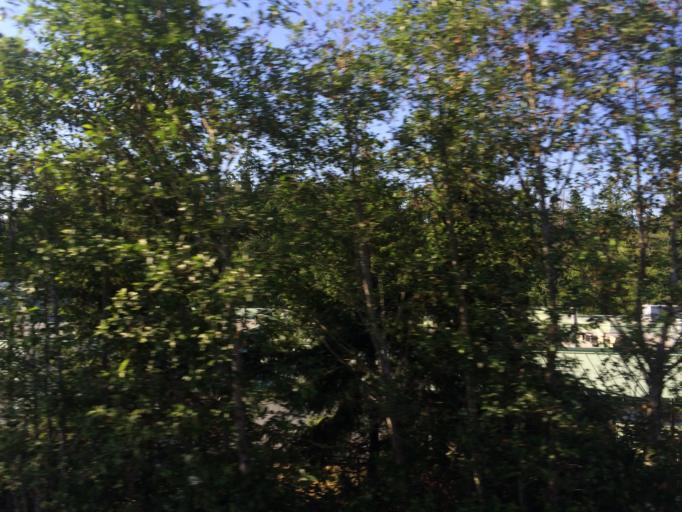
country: CA
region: British Columbia
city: Colwood
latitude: 48.4627
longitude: -123.4429
